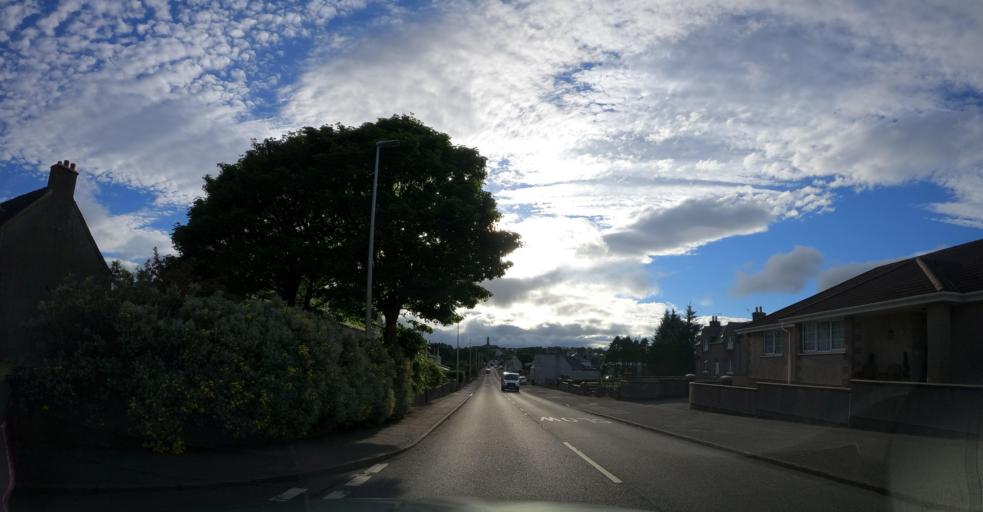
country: GB
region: Scotland
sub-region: Eilean Siar
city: Isle of Lewis
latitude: 58.2185
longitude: -6.3801
